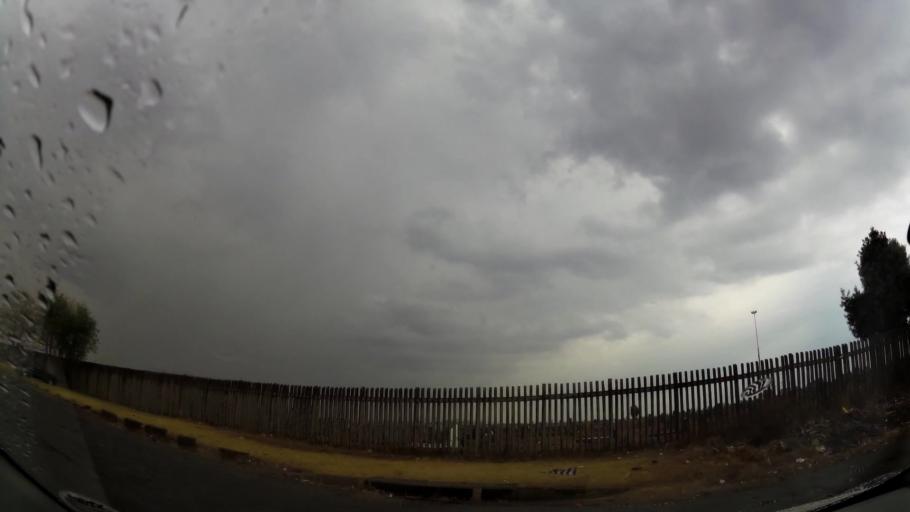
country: ZA
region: Gauteng
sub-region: Ekurhuleni Metropolitan Municipality
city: Germiston
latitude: -26.3719
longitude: 28.1402
